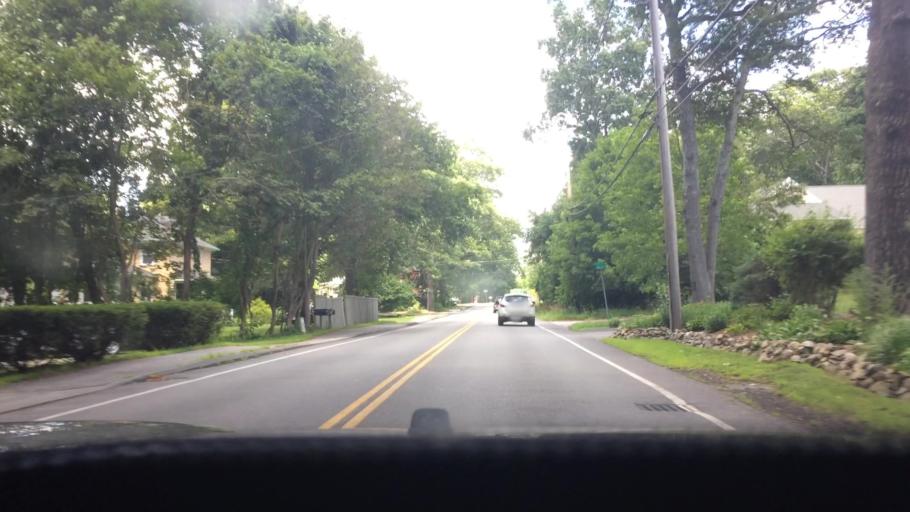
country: US
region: Massachusetts
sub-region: Middlesex County
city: Maynard
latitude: 42.4525
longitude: -71.4545
